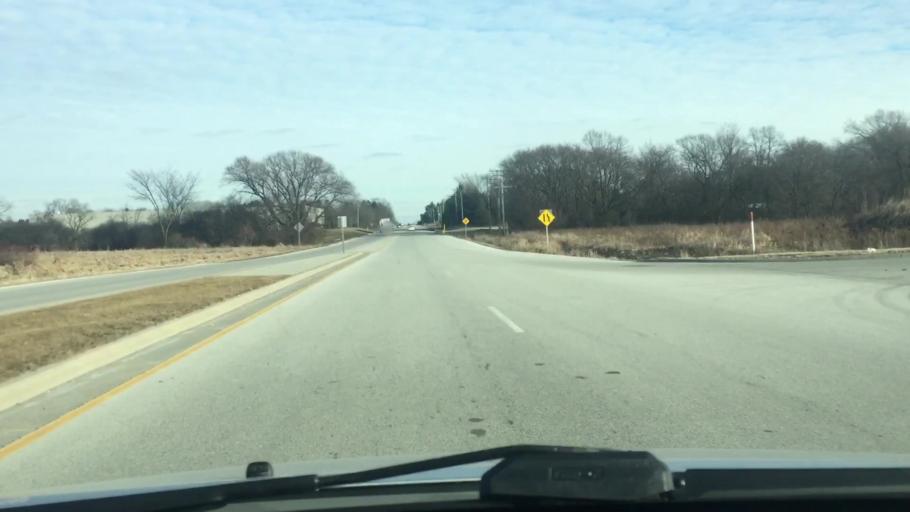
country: US
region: Wisconsin
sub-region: Waukesha County
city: Sussex
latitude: 43.1121
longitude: -88.2394
